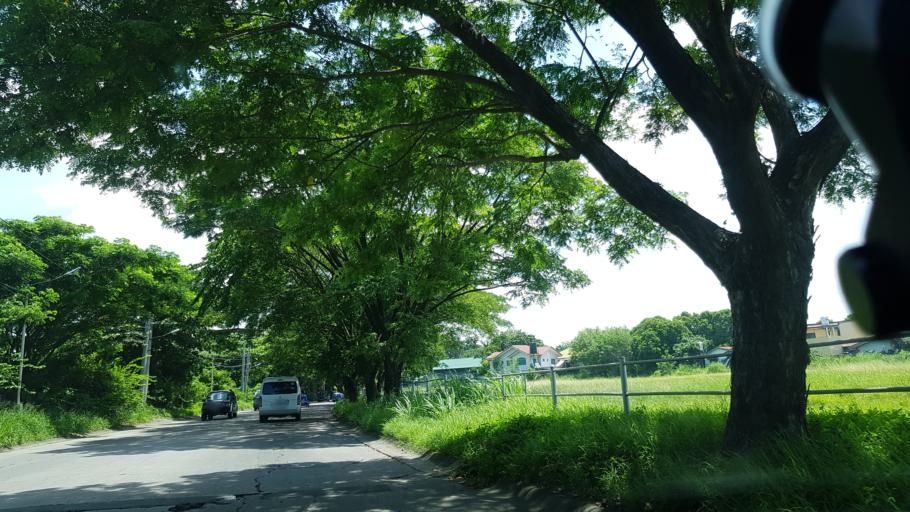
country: PH
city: Sambayanihan People's Village
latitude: 14.4463
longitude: 121.0111
